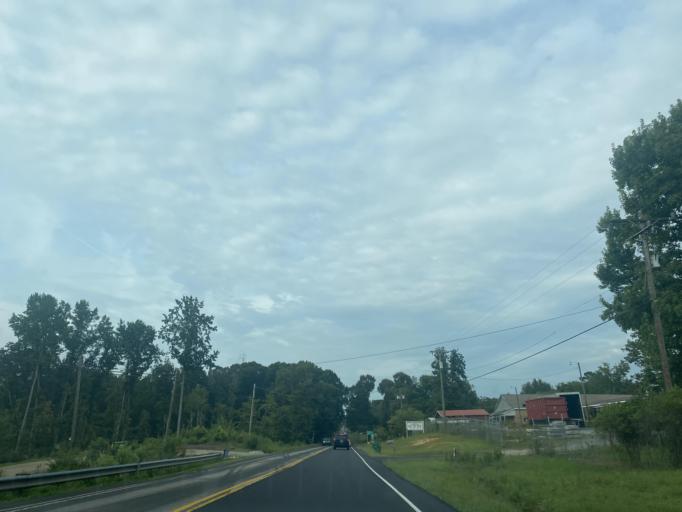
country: US
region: South Carolina
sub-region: Cherokee County
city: Blacksburg
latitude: 35.0978
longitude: -81.5490
